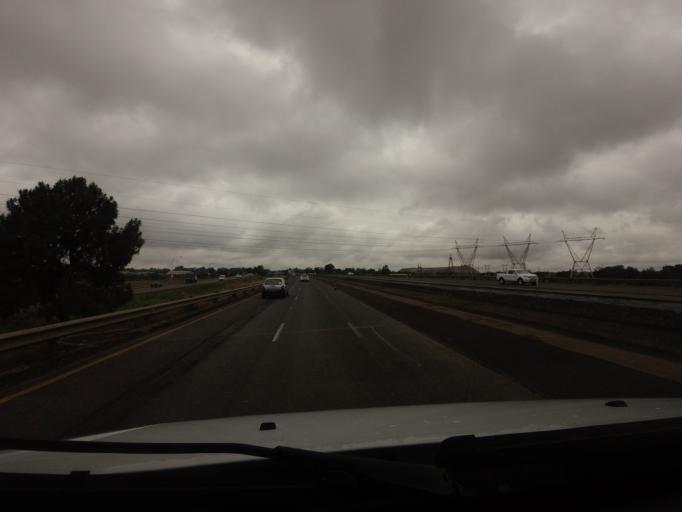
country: ZA
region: Mpumalanga
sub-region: Nkangala District Municipality
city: Witbank
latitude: -25.8846
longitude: 29.1987
